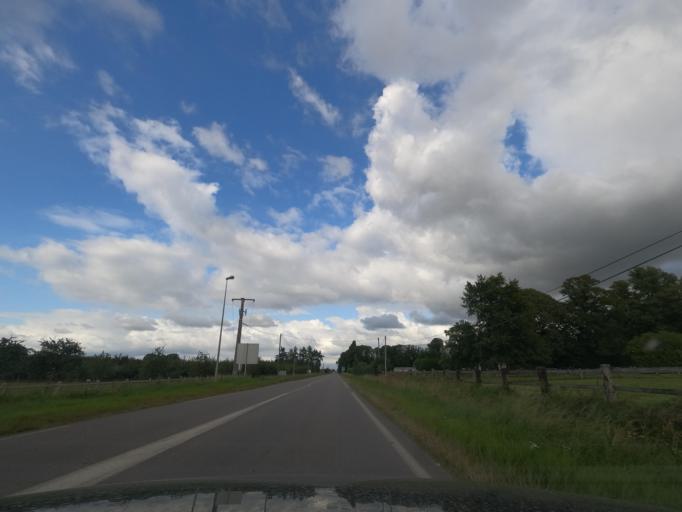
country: FR
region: Lower Normandy
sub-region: Departement du Calvados
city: Orbec
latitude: 48.9567
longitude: 0.4673
